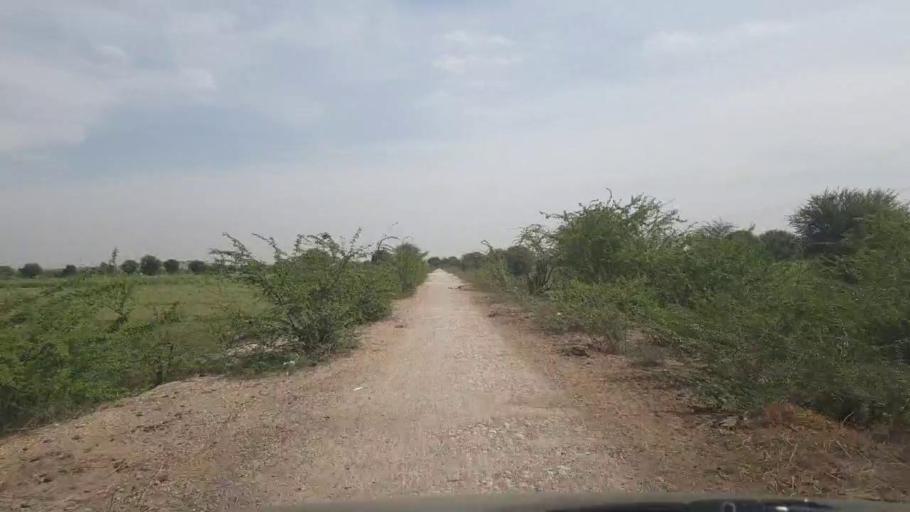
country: PK
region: Sindh
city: Kunri
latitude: 25.1976
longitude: 69.6830
